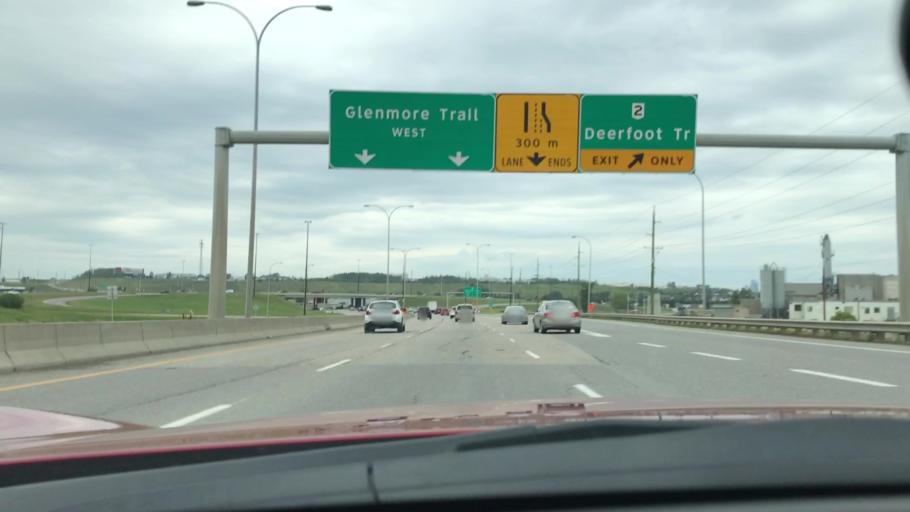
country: CA
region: Alberta
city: Calgary
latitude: 50.9904
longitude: -114.0294
